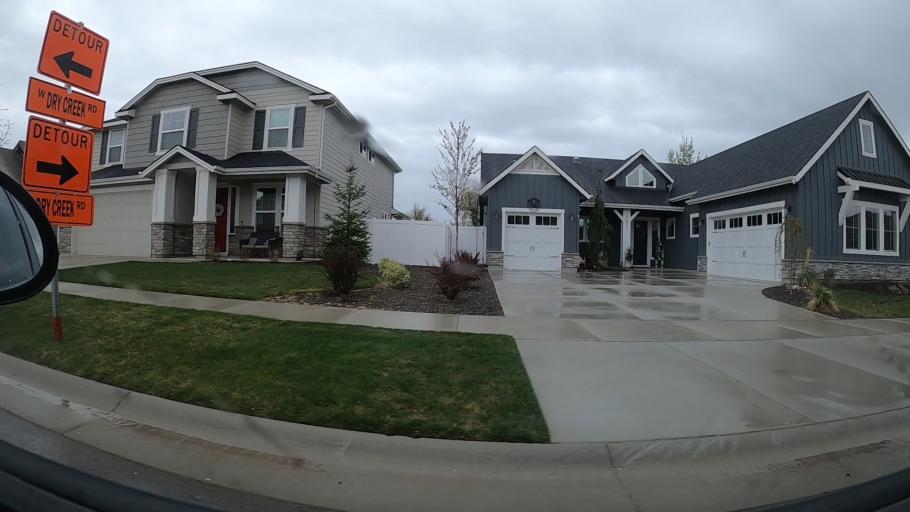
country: US
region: Idaho
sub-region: Ada County
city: Eagle
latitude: 43.7326
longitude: -116.2958
